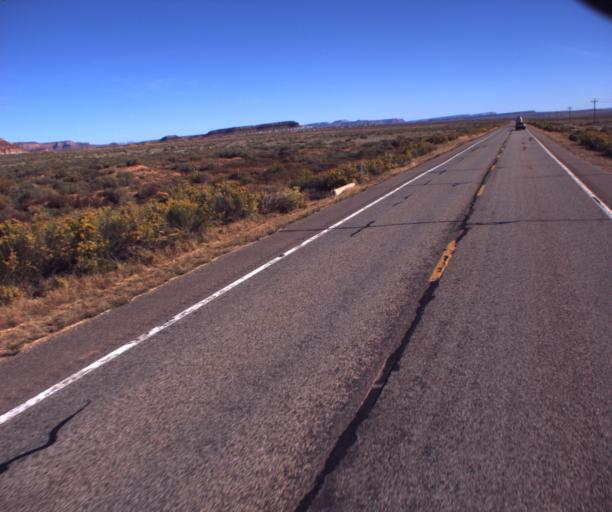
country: US
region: Arizona
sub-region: Coconino County
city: Fredonia
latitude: 36.8821
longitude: -112.6392
